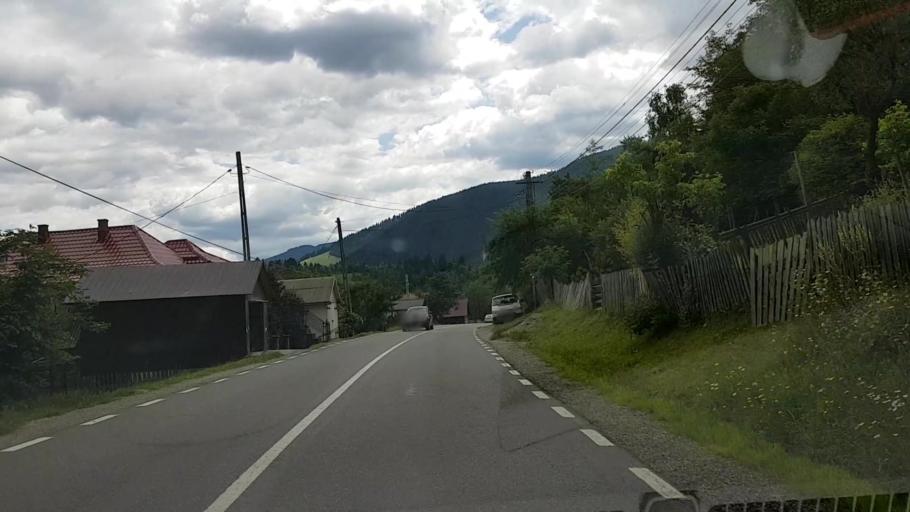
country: RO
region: Neamt
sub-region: Comuna Borca
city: Borca
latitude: 47.2137
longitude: 25.7559
